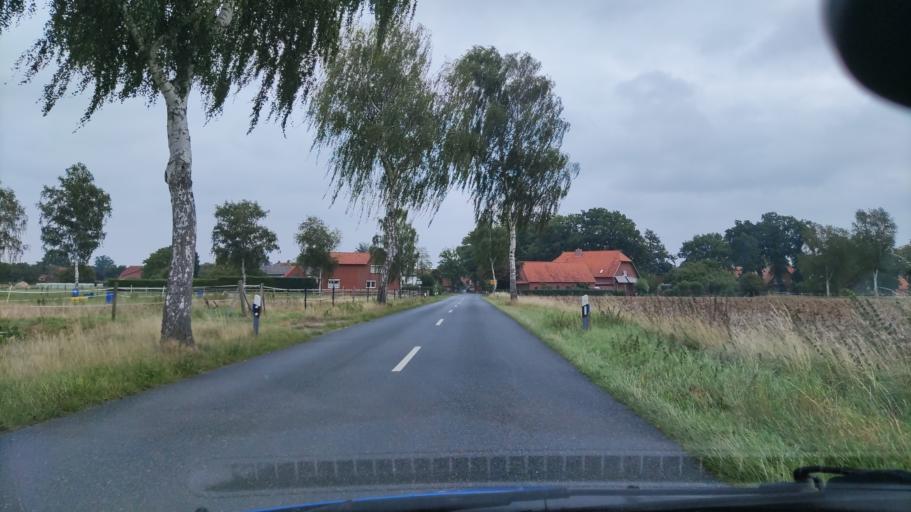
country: DE
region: Lower Saxony
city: Bienenbuttel
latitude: 53.1448
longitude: 10.5294
